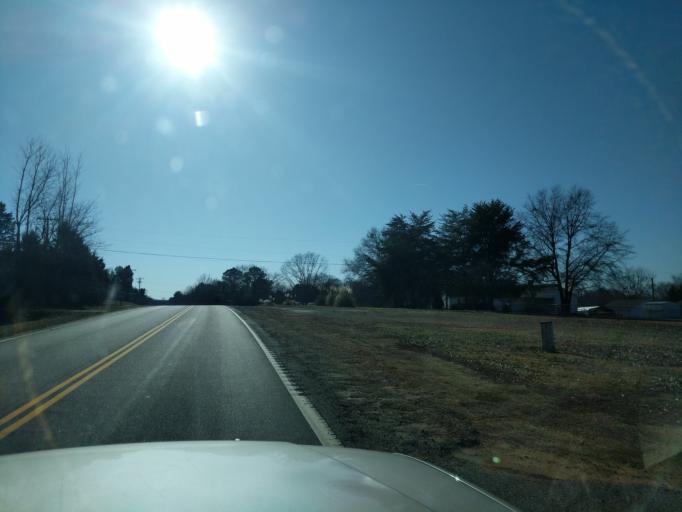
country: US
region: South Carolina
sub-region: Anderson County
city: Homeland Park
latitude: 34.4295
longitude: -82.7477
